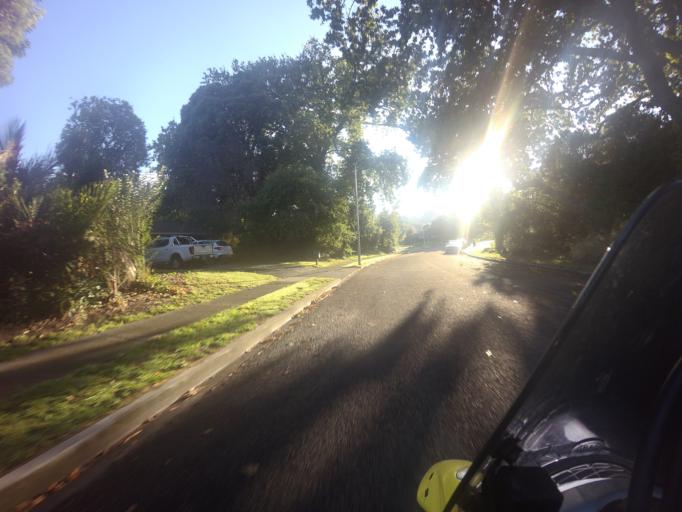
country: NZ
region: Gisborne
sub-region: Gisborne District
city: Gisborne
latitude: -38.6642
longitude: 178.0518
